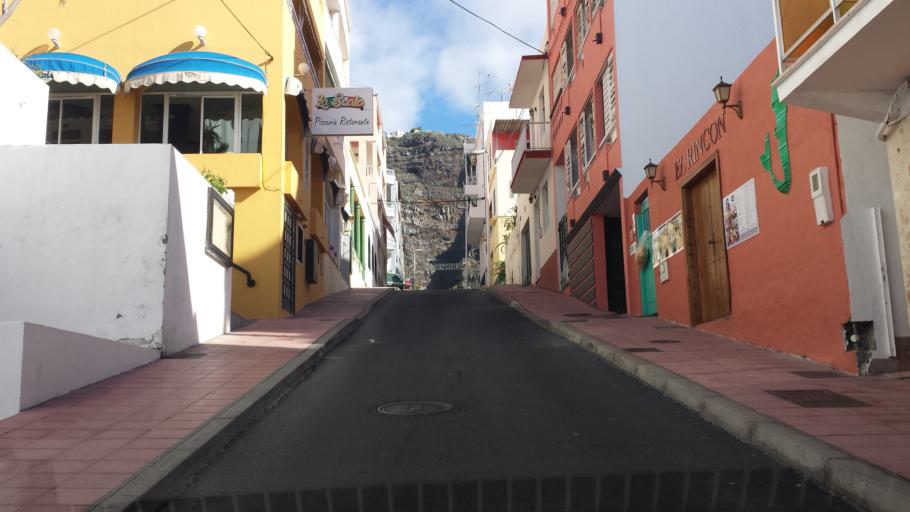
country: ES
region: Canary Islands
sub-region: Provincia de Santa Cruz de Tenerife
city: Tazacorte
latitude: 28.5868
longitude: -17.9107
